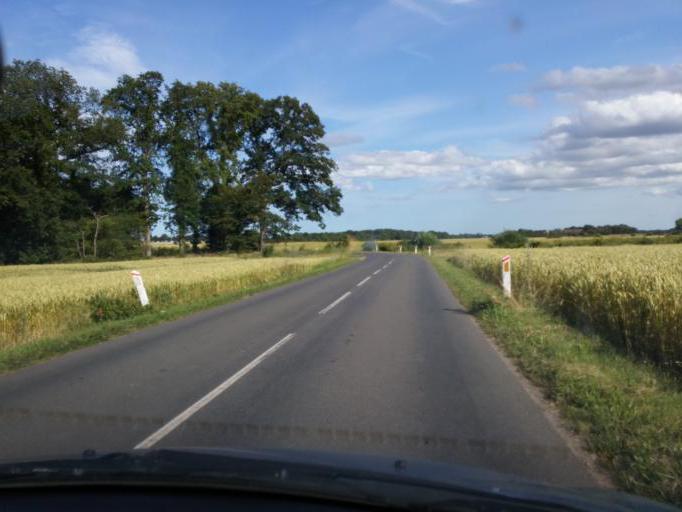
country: DK
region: South Denmark
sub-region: Kerteminde Kommune
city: Munkebo
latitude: 55.4236
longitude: 10.5452
